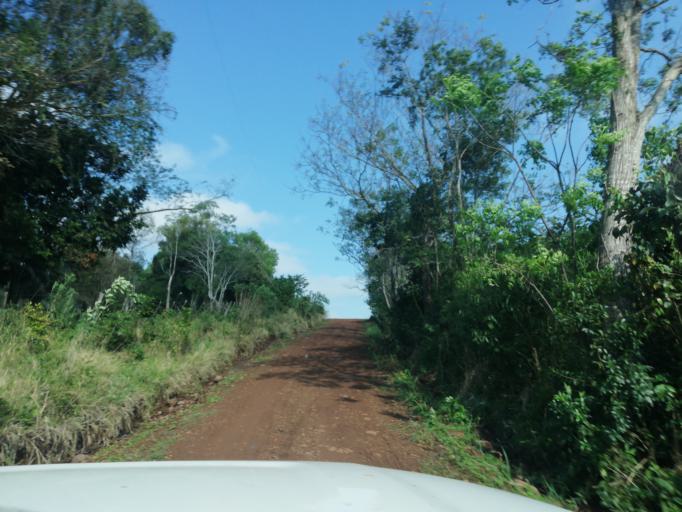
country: AR
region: Misiones
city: Cerro Azul
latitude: -27.5989
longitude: -55.5270
